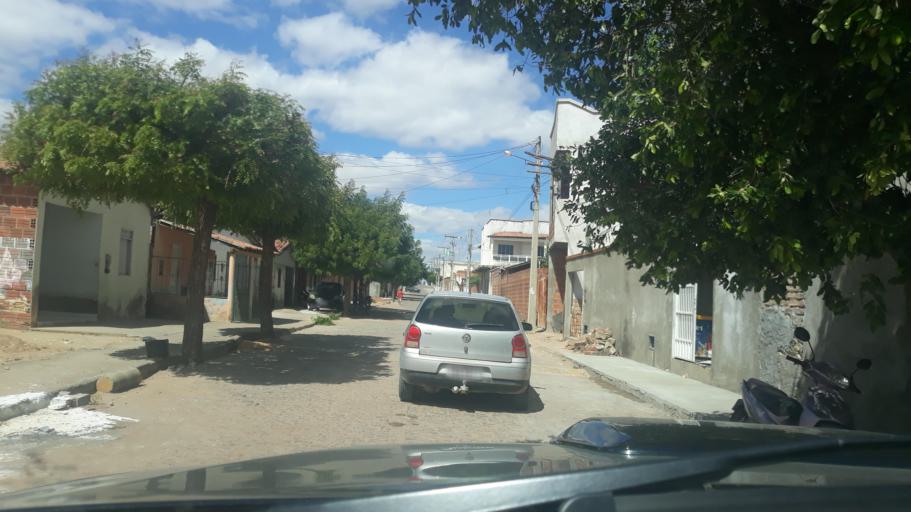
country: BR
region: Bahia
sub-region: Riacho De Santana
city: Riacho de Santana
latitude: -13.9081
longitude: -42.8481
